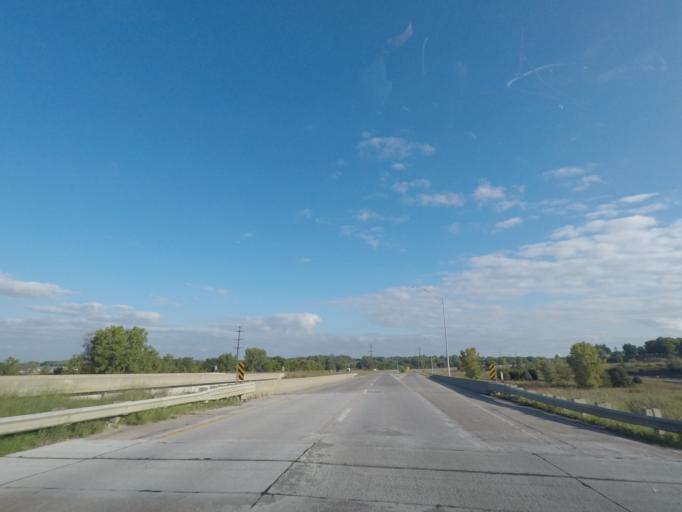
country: US
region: Iowa
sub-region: Polk County
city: Pleasant Hill
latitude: 41.5718
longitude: -93.5131
